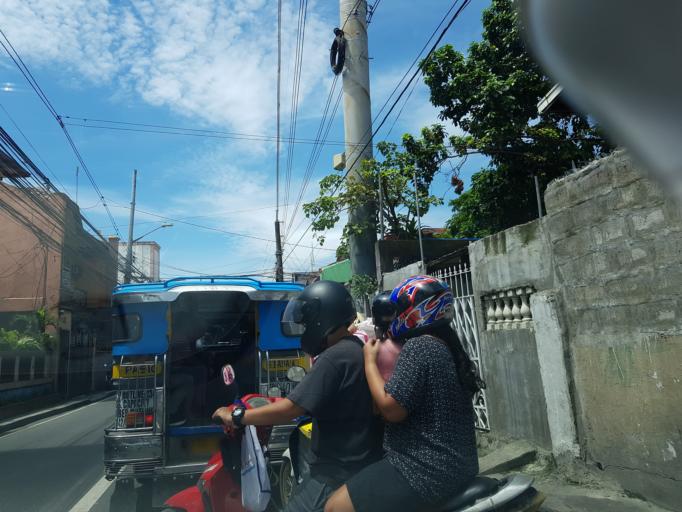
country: PH
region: Calabarzon
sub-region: Province of Rizal
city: Taguig
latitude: 14.5112
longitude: 121.0688
